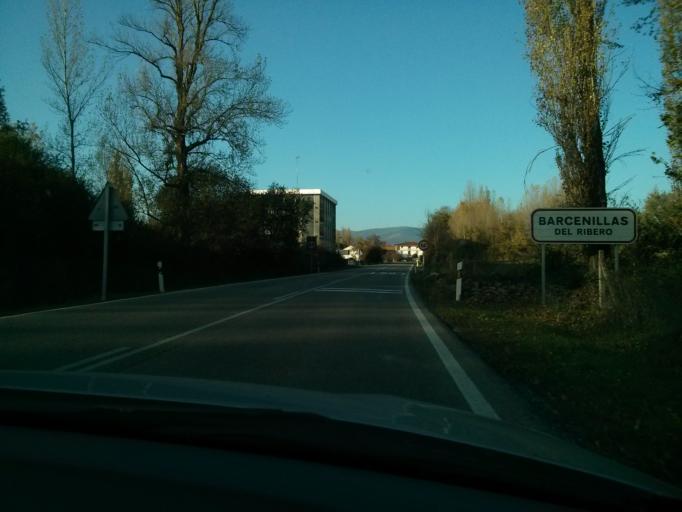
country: ES
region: Castille and Leon
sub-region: Provincia de Burgos
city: Espinosa de los Monteros
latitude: 43.0232
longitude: -3.4841
